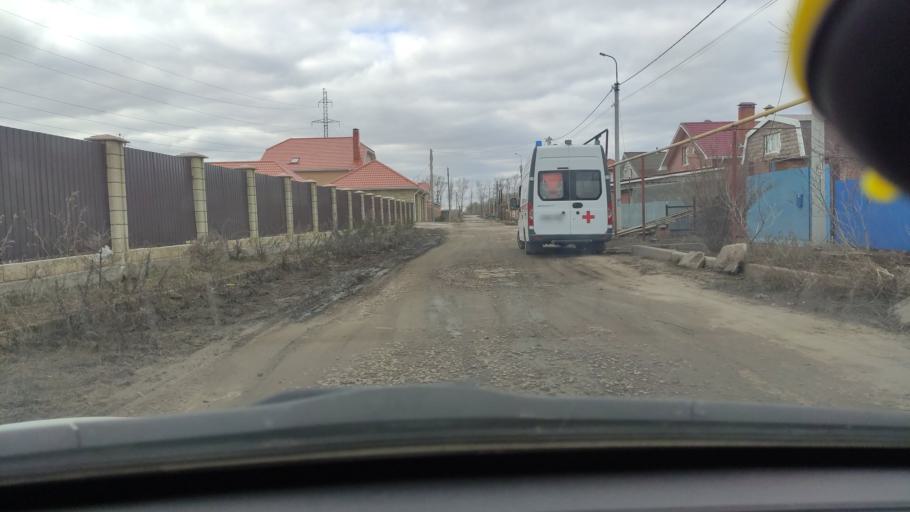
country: RU
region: Samara
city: Tol'yatti
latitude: 53.5500
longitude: 49.3988
